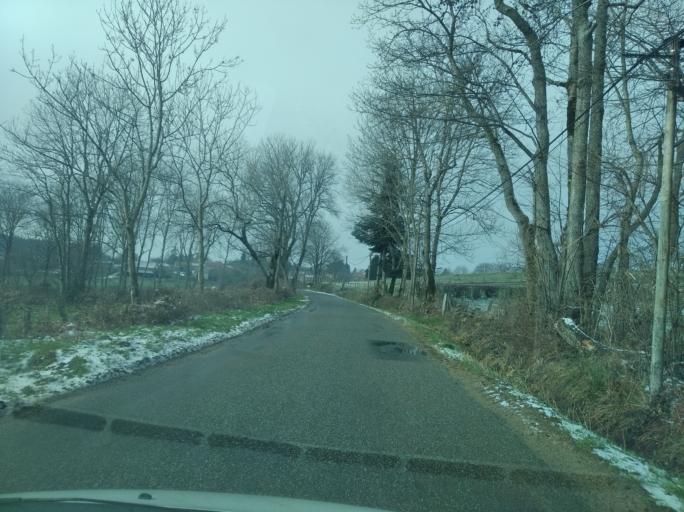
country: FR
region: Rhone-Alpes
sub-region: Departement de la Loire
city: Ambierle
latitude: 46.1144
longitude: 3.8012
